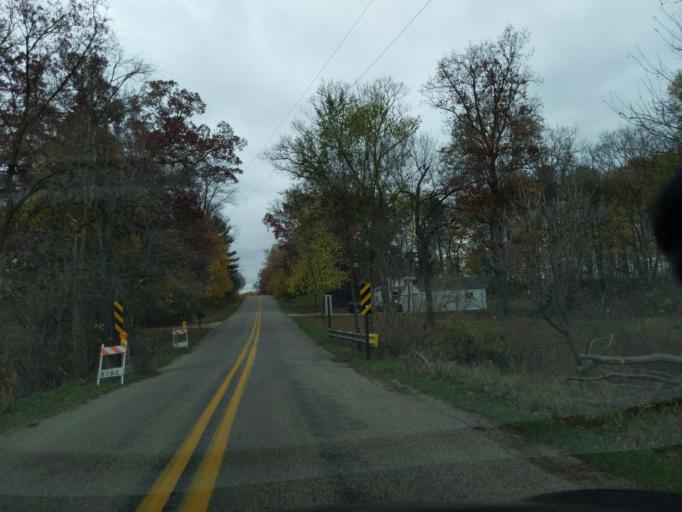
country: US
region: Michigan
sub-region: Eaton County
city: Eaton Rapids
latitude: 42.4984
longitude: -84.6012
